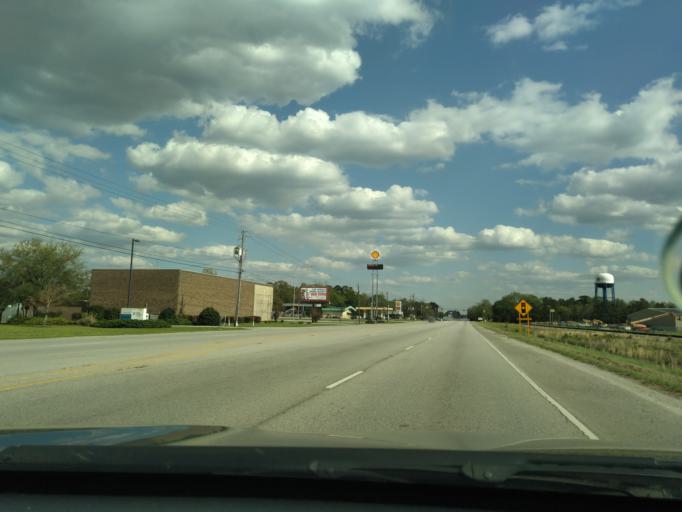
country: US
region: South Carolina
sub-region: Florence County
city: Florence
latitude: 34.2238
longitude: -79.7922
